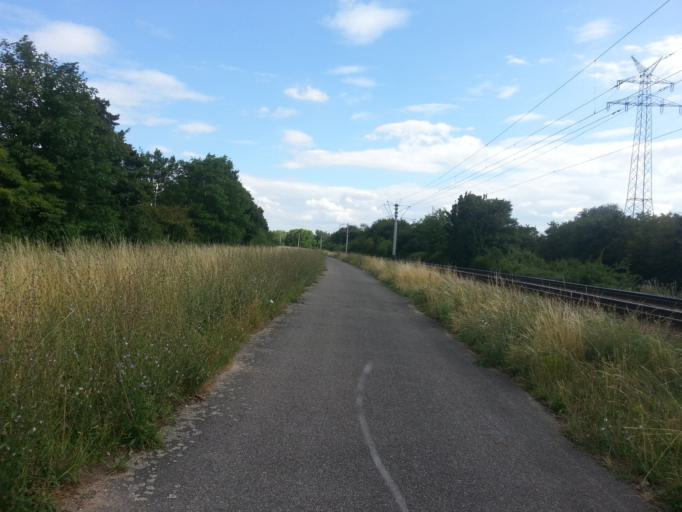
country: DE
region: Baden-Wuerttemberg
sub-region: Karlsruhe Region
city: Ilvesheim
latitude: 49.5030
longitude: 8.5334
